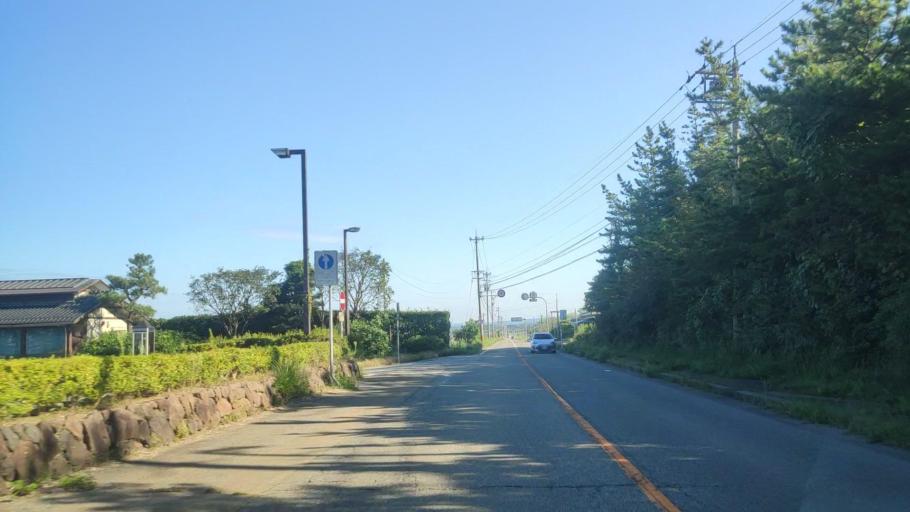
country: JP
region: Ishikawa
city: Hakui
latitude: 36.9332
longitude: 136.7565
